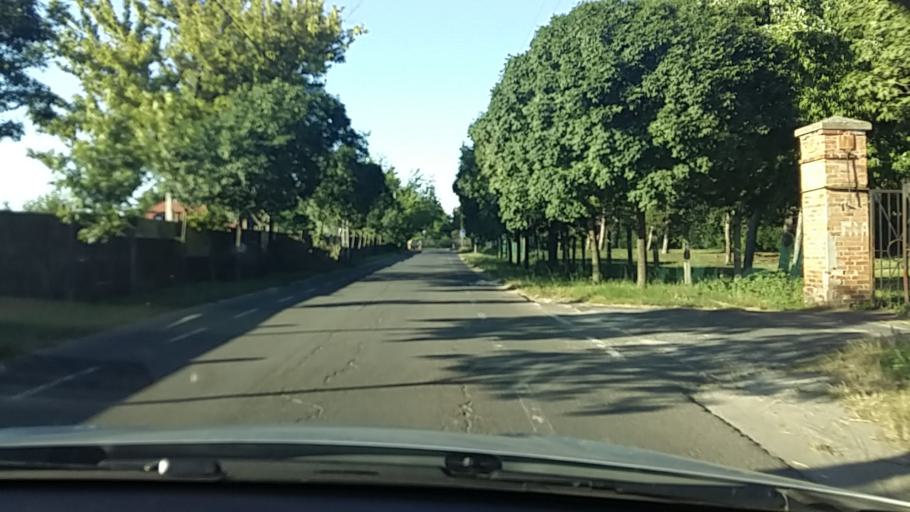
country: HU
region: Pest
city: Dunakeszi
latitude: 47.6271
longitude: 19.1454
